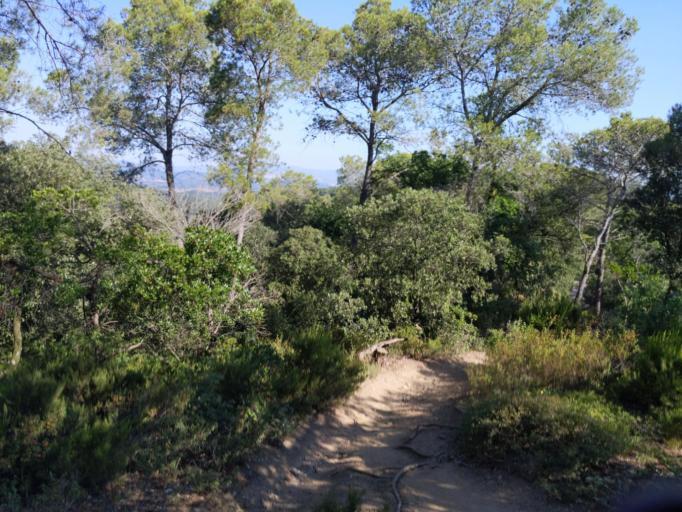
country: ES
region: Catalonia
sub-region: Provincia de Barcelona
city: Cerdanyola del Valles
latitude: 41.4533
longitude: 2.1373
